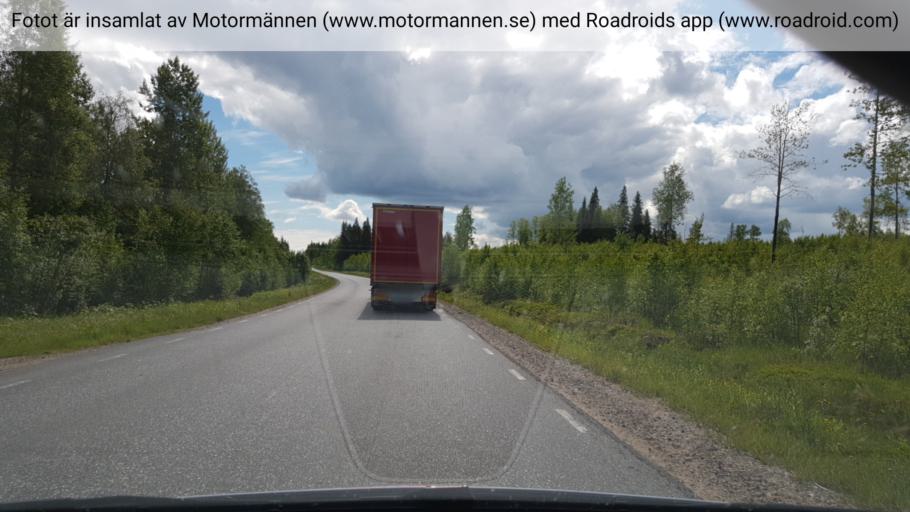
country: FI
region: Lapland
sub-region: Torniolaakso
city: Ylitornio
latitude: 66.2580
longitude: 23.6558
